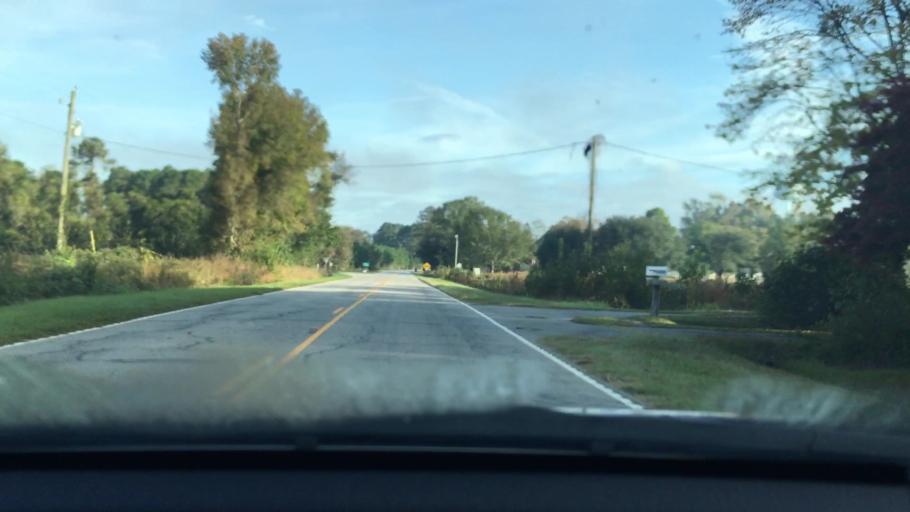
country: US
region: South Carolina
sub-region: Sumter County
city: East Sumter
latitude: 34.0045
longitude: -80.2877
